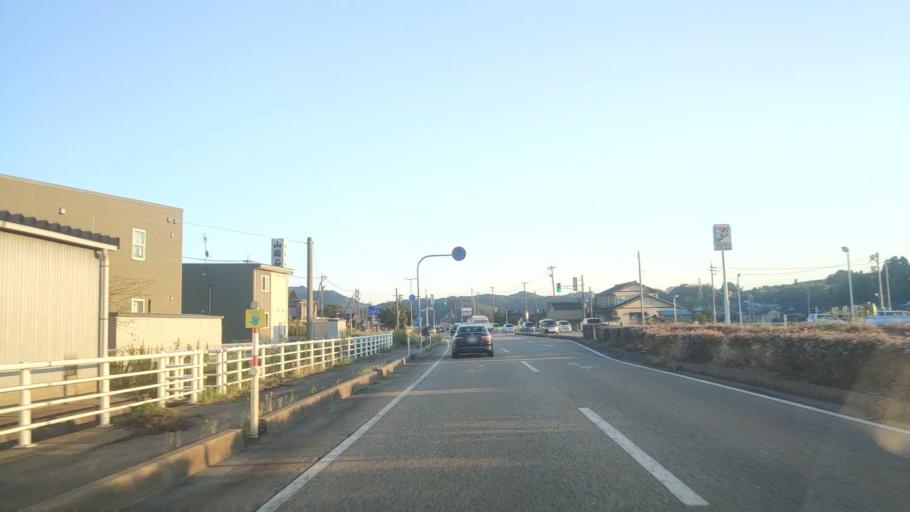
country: JP
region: Toyama
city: Himi
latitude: 36.8188
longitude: 136.9949
